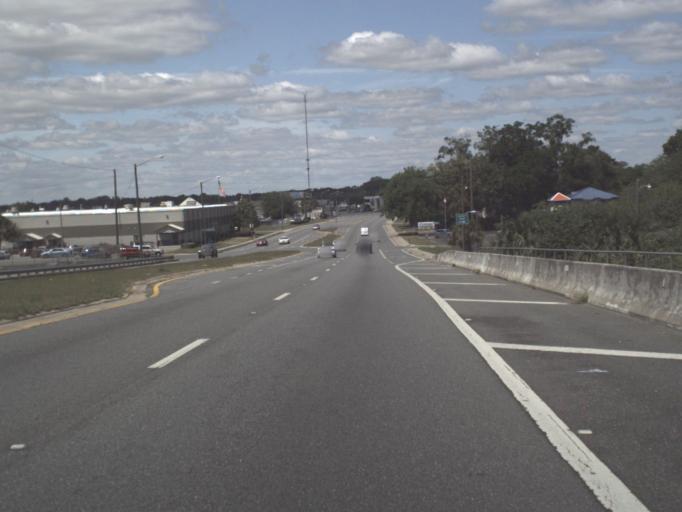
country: US
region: Florida
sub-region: Marion County
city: Ocala
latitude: 29.1791
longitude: -82.1457
